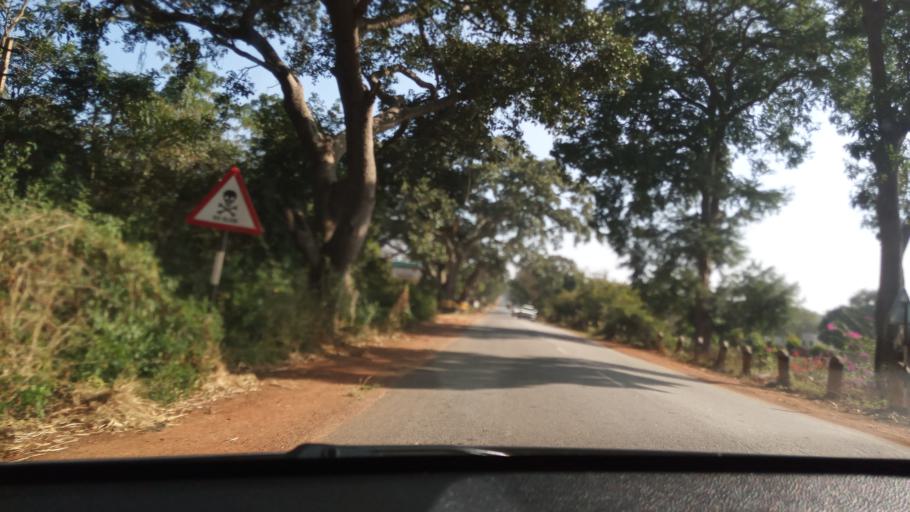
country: IN
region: Karnataka
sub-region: Bangalore Rural
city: Devanhalli
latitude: 13.2647
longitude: 77.7381
